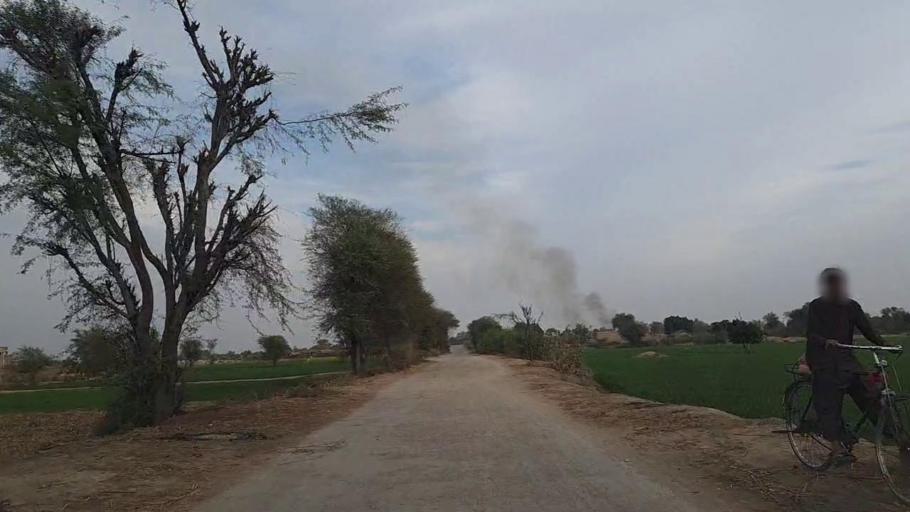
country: PK
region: Sindh
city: Daur
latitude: 26.5279
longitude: 68.4288
